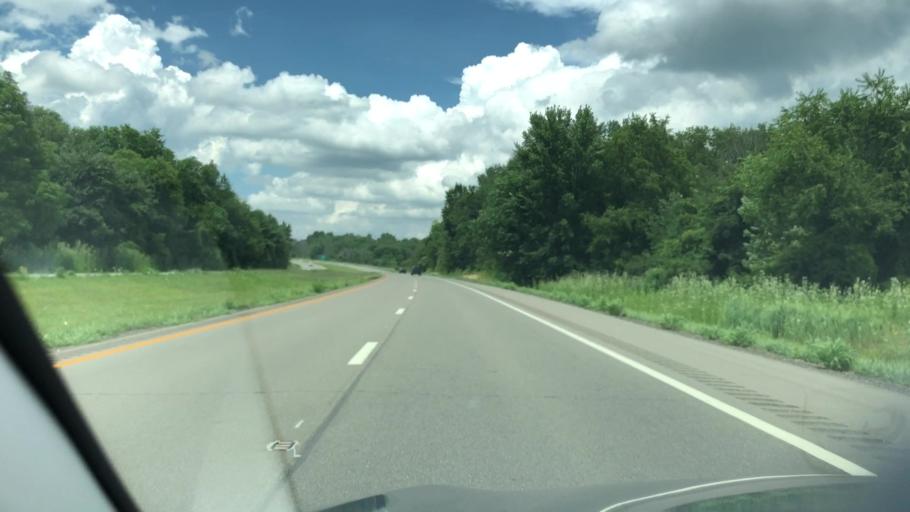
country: US
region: Ohio
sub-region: Stark County
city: Canal Fulton
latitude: 40.8620
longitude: -81.5818
